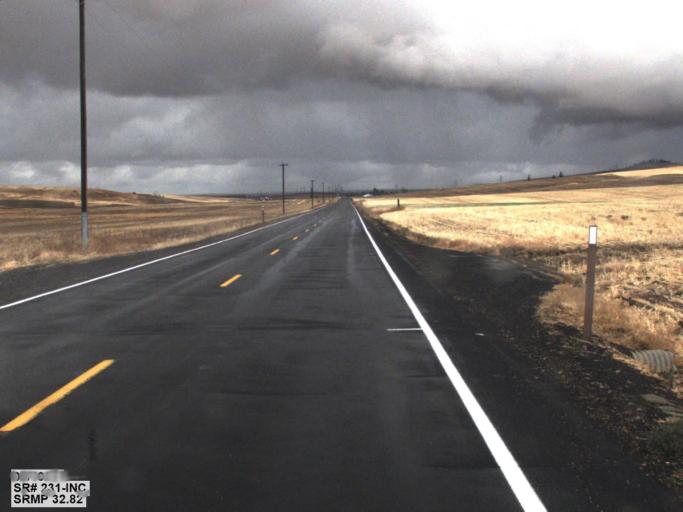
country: US
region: Washington
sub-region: Spokane County
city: Medical Lake
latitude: 47.6941
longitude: -117.8810
